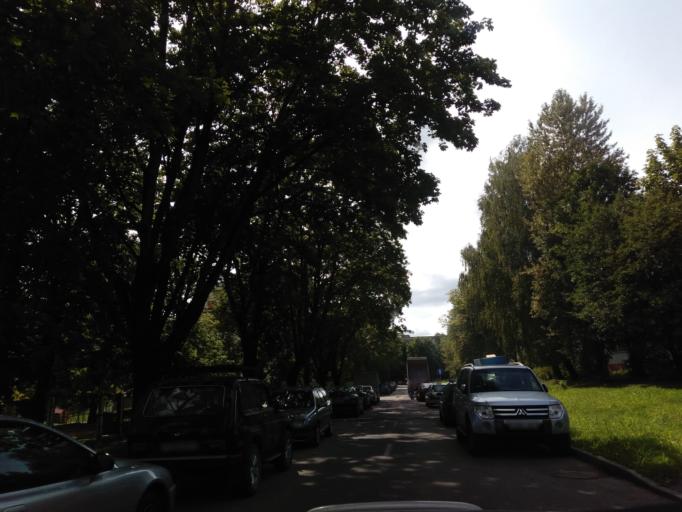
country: BY
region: Minsk
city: Novoye Medvezhino
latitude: 53.8770
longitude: 27.5017
